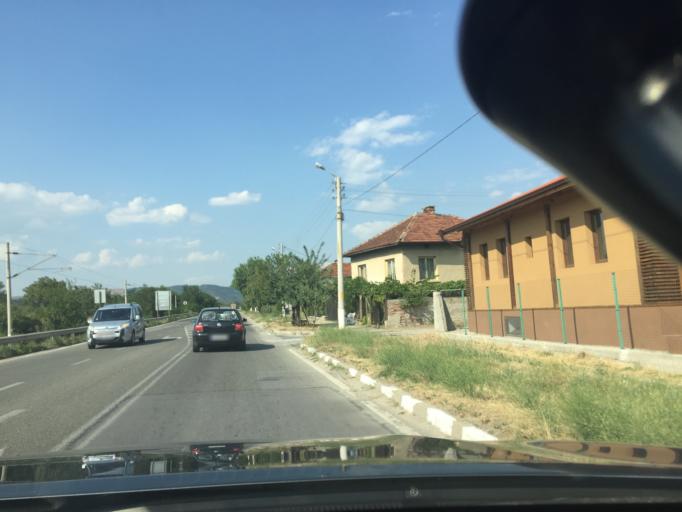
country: BG
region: Kyustendil
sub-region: Obshtina Dupnitsa
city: Dupnitsa
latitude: 42.2264
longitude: 23.0810
